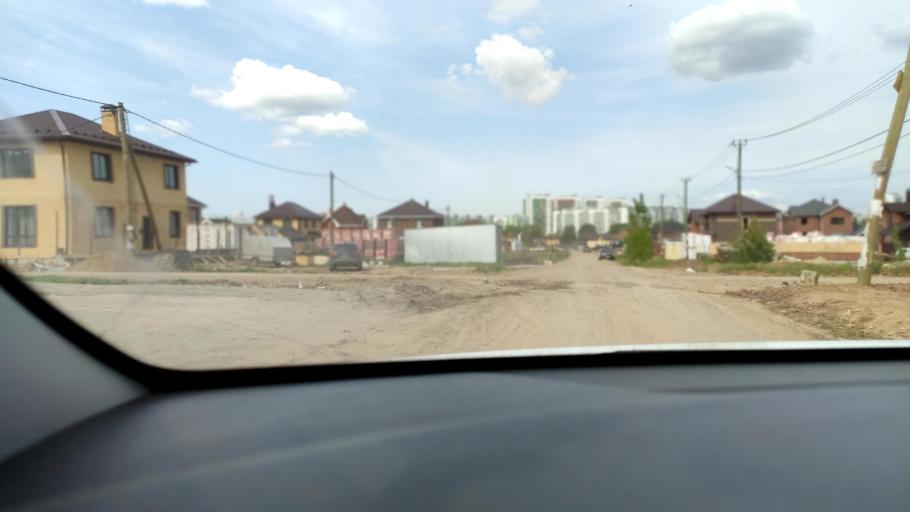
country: RU
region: Tatarstan
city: Vysokaya Gora
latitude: 55.7904
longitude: 49.2643
